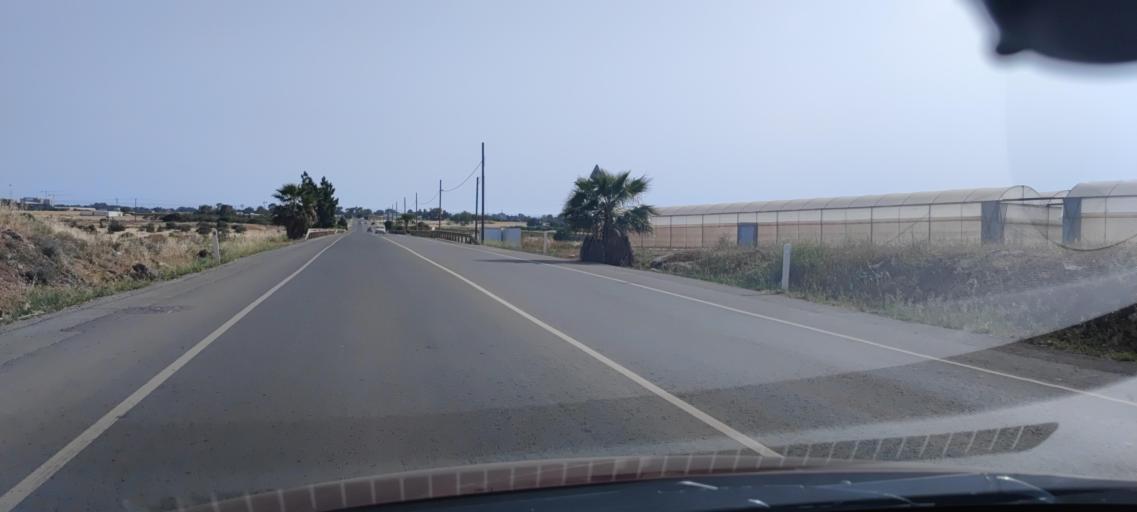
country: CY
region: Ammochostos
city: Frenaros
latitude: 35.0018
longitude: 33.9358
